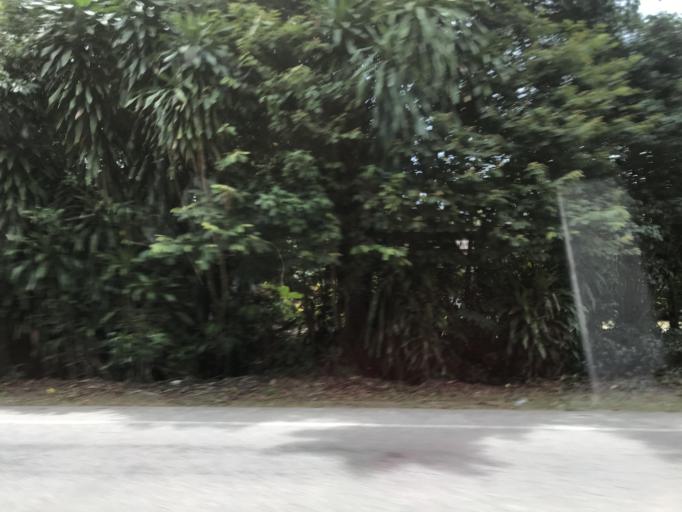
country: MY
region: Kelantan
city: Tumpat
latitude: 6.1767
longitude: 102.1915
